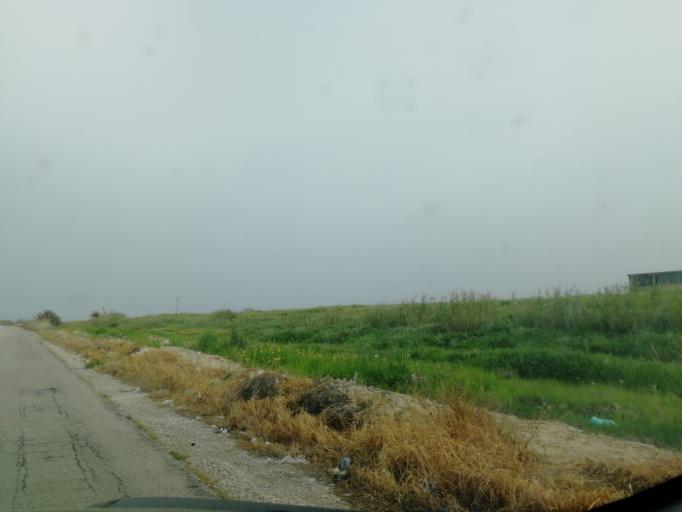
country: IT
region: Apulia
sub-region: Provincia di Barletta - Andria - Trani
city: Barletta
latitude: 41.3181
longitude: 16.3052
